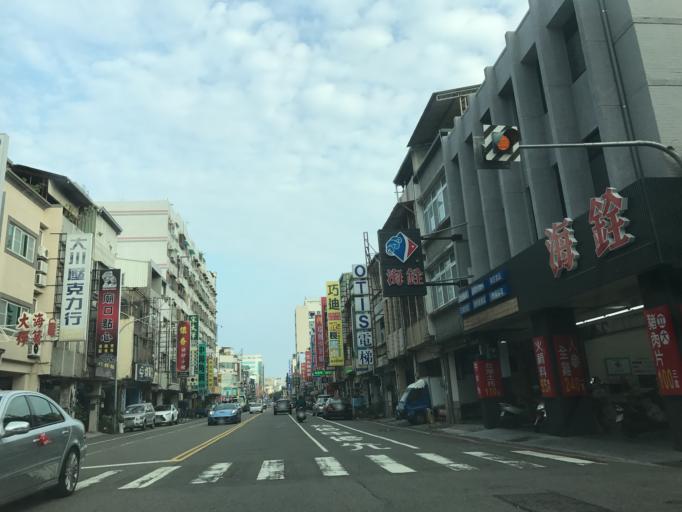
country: TW
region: Taiwan
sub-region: Tainan
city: Tainan
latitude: 22.9996
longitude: 120.1937
